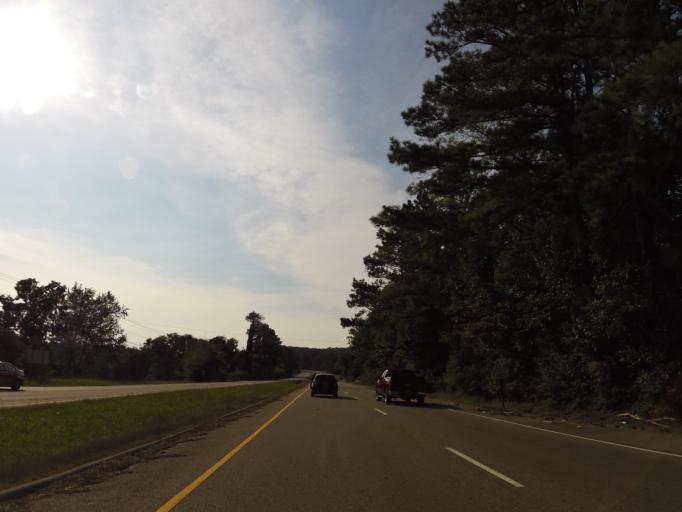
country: US
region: Tennessee
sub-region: Loudon County
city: Lenoir City
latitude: 35.8372
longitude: -84.2929
